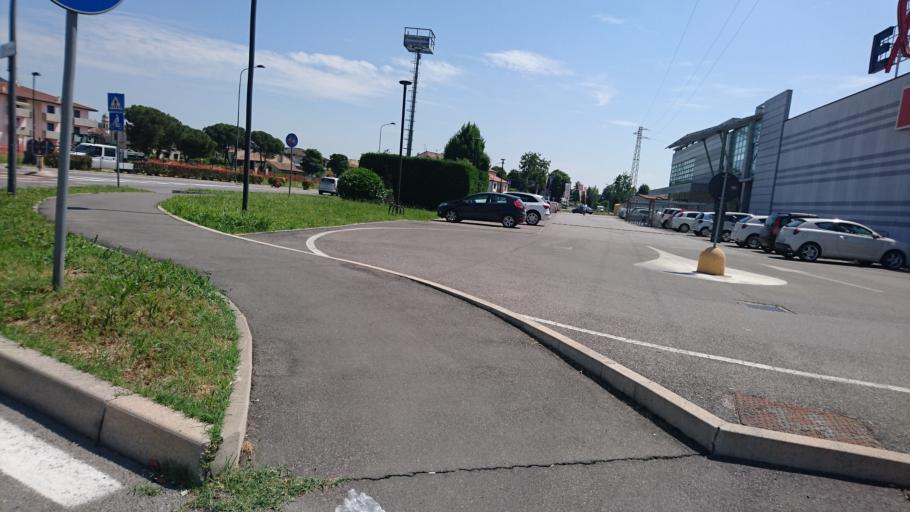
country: IT
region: Veneto
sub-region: Provincia di Padova
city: Este
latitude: 45.2248
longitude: 11.6430
